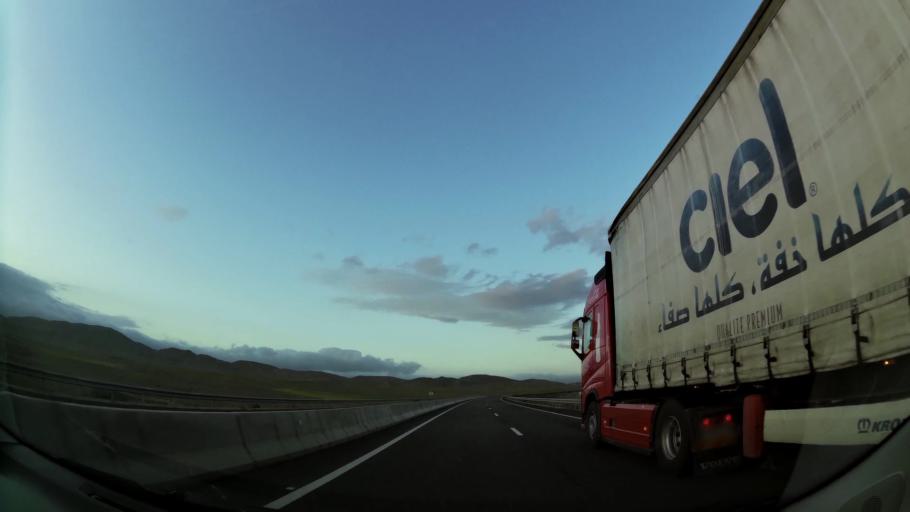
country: MA
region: Oriental
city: Taourirt
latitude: 34.5822
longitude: -2.8058
